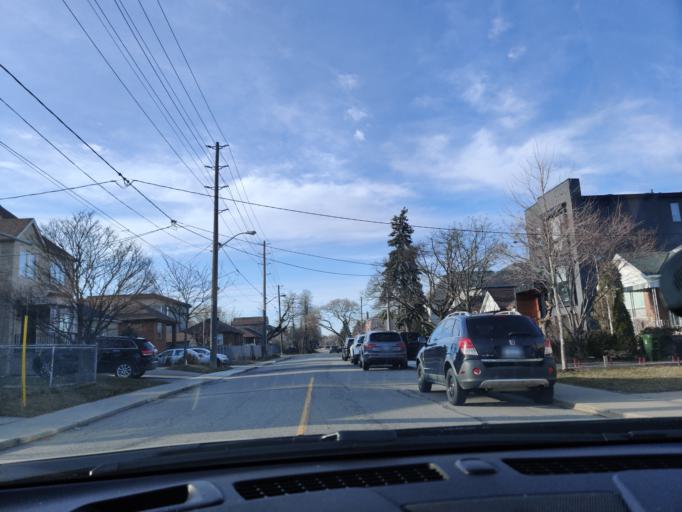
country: CA
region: Ontario
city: Toronto
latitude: 43.7033
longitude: -79.4443
